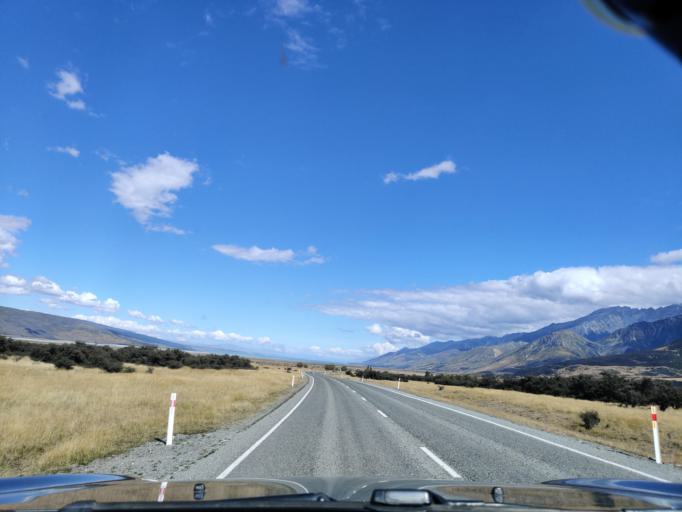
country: NZ
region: Canterbury
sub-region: Timaru District
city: Pleasant Point
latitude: -43.7791
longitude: 170.1237
